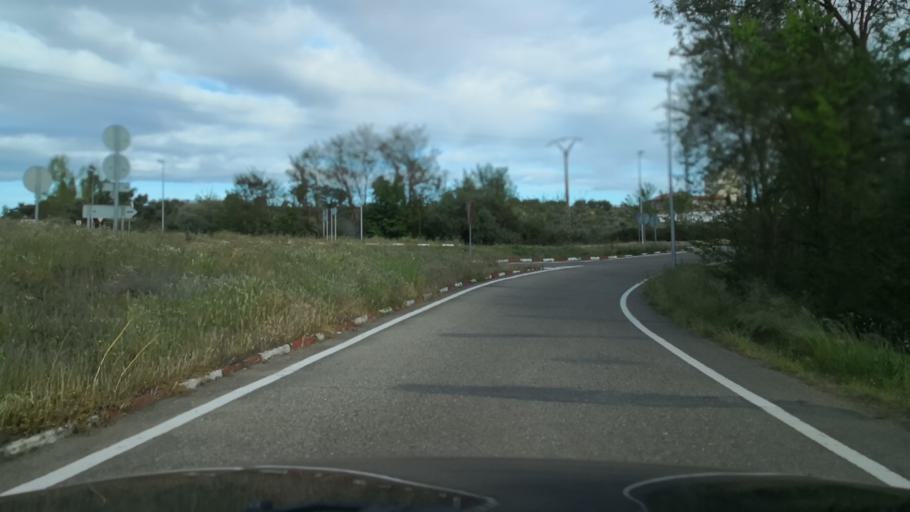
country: ES
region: Extremadura
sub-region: Provincia de Caceres
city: Coria
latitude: 39.9960
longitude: -6.5428
